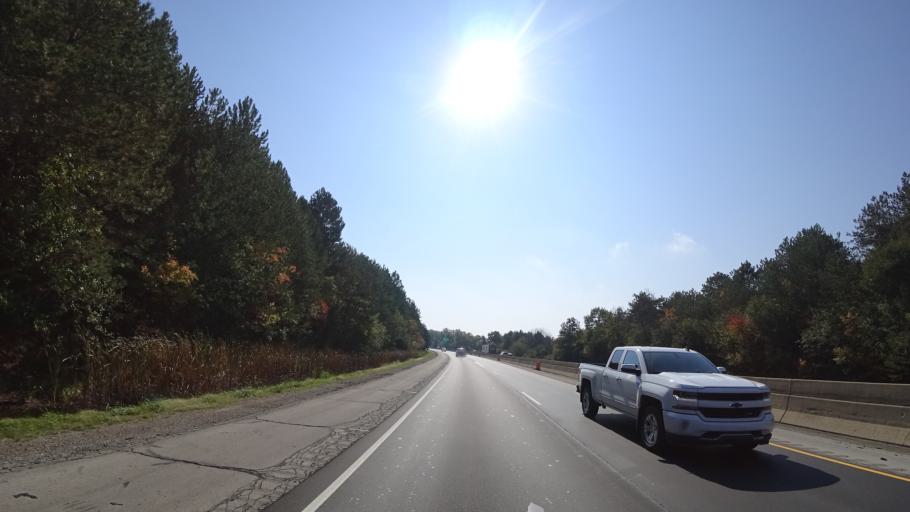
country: US
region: Michigan
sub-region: Washtenaw County
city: Ann Arbor
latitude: 42.2661
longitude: -83.7846
